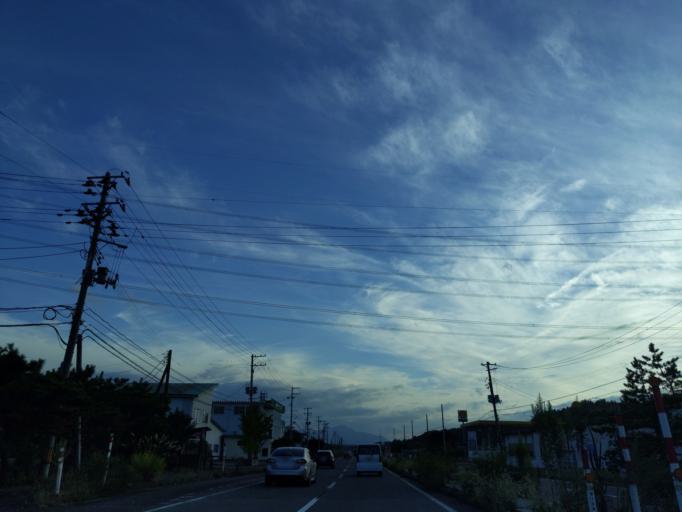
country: JP
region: Niigata
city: Kashiwazaki
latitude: 37.4434
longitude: 138.6333
